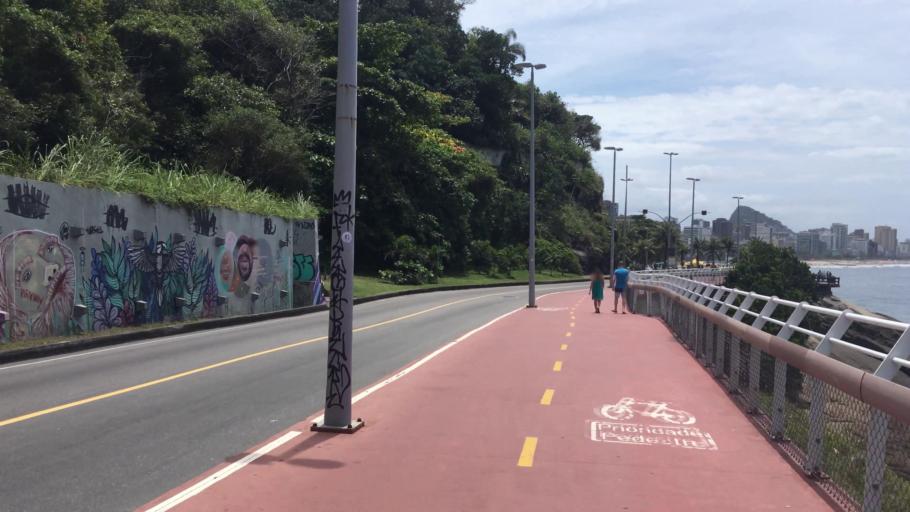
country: BR
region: Rio de Janeiro
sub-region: Rio De Janeiro
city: Rio de Janeiro
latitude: -22.9905
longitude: -43.2289
